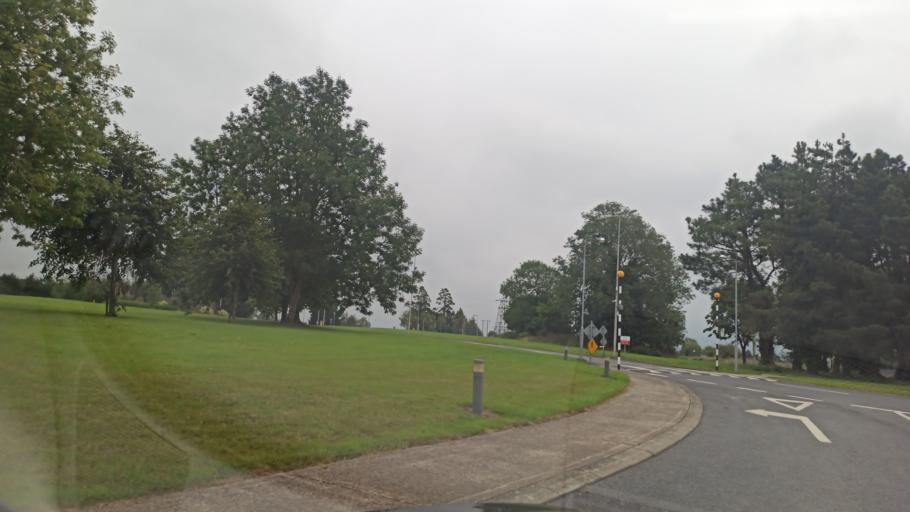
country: IE
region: Munster
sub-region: South Tipperary
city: Cluain Meala
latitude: 52.3711
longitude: -7.7212
